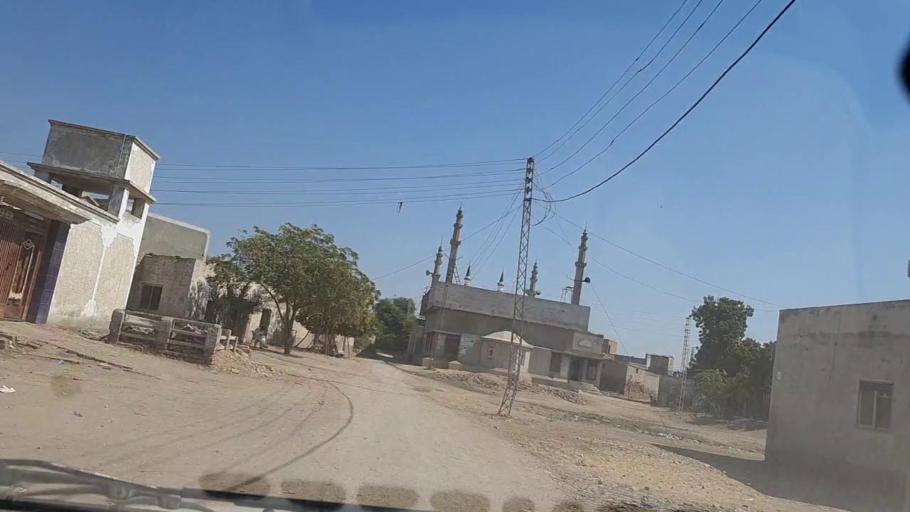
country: PK
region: Sindh
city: Mirpur Khas
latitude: 25.4344
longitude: 69.0168
